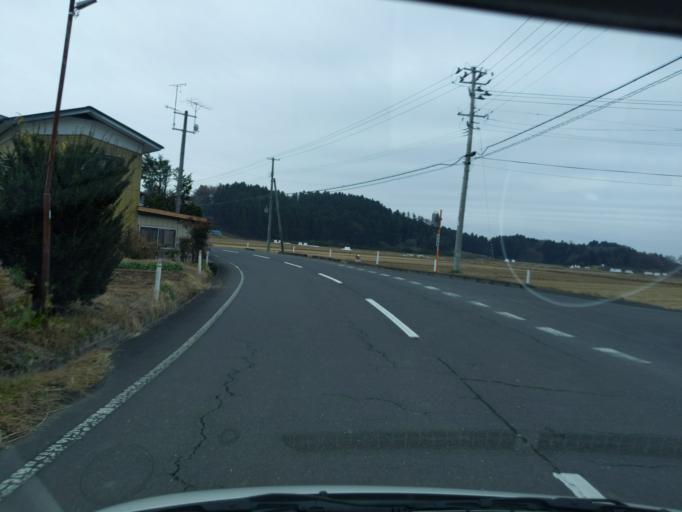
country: JP
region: Iwate
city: Ichinoseki
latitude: 38.7342
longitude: 141.2199
